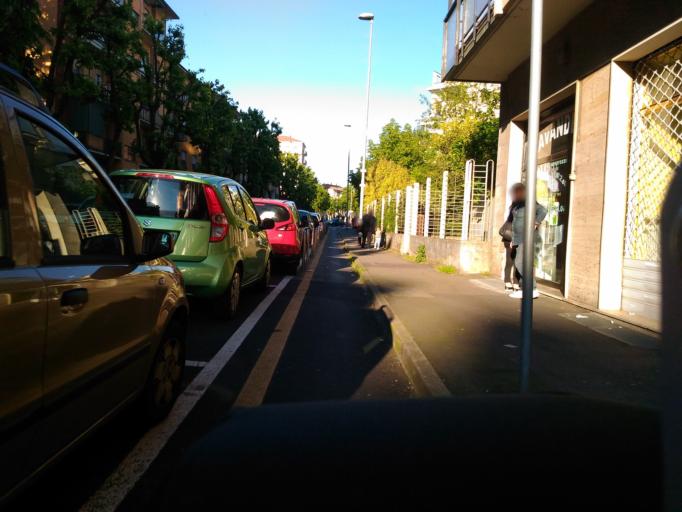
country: IT
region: Lombardy
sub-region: Provincia di Lodi
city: Lodi
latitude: 45.3118
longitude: 9.4937
